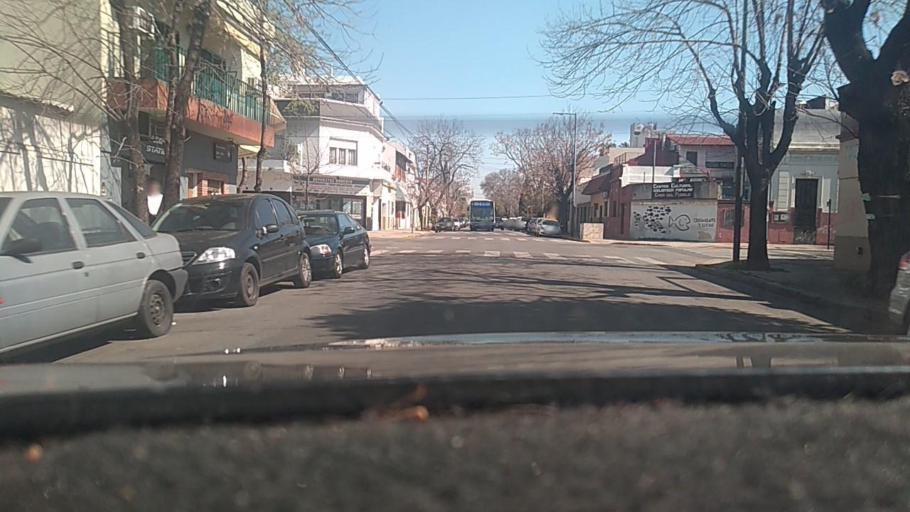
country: AR
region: Buenos Aires F.D.
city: Villa Santa Rita
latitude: -34.6084
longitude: -58.4967
